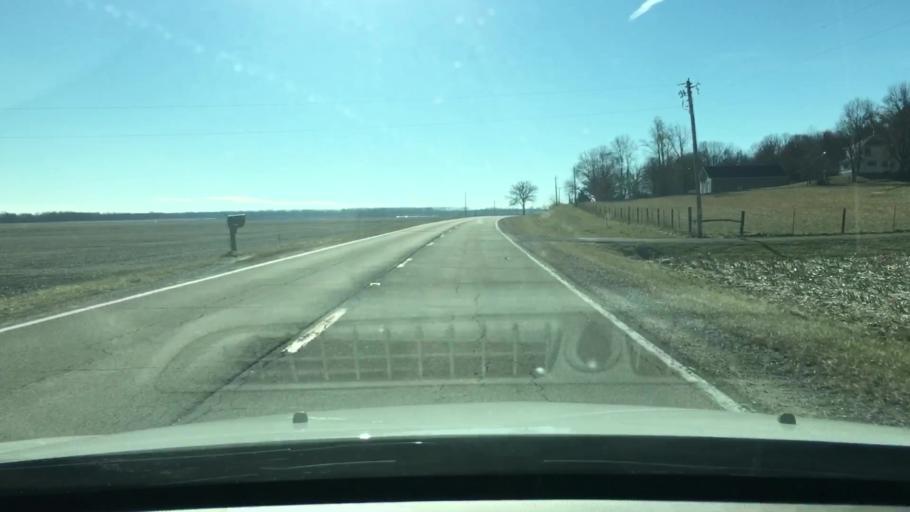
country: US
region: Illinois
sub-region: Mason County
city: Havana
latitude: 40.2611
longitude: -90.1774
